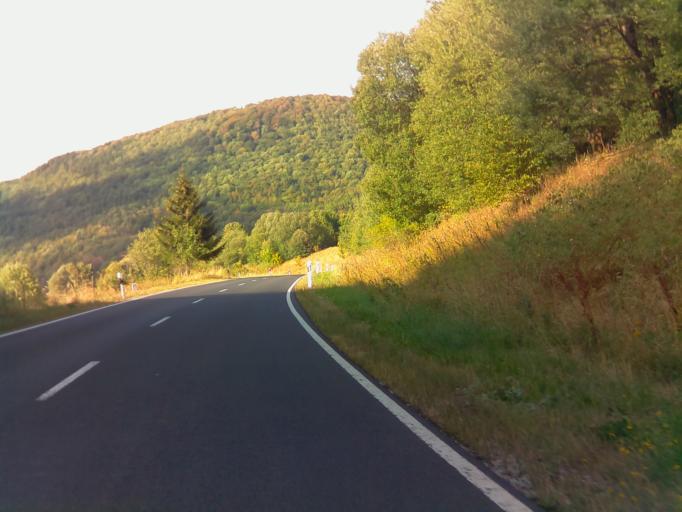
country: DE
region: Thuringia
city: Birx
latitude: 50.5158
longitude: 10.0353
